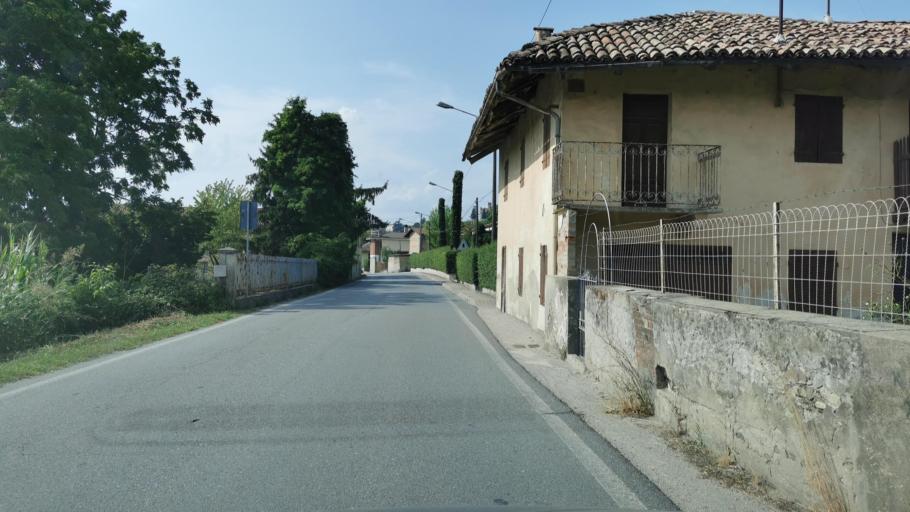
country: IT
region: Piedmont
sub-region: Provincia di Cuneo
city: Grinzane Cavour
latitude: 44.6441
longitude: 7.9991
